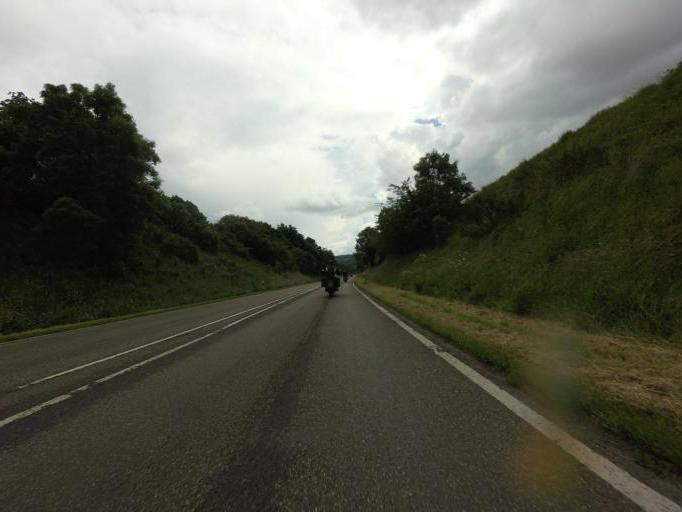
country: DE
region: Rheinland-Pfalz
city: Kaisersesch
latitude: 50.2325
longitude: 7.1468
